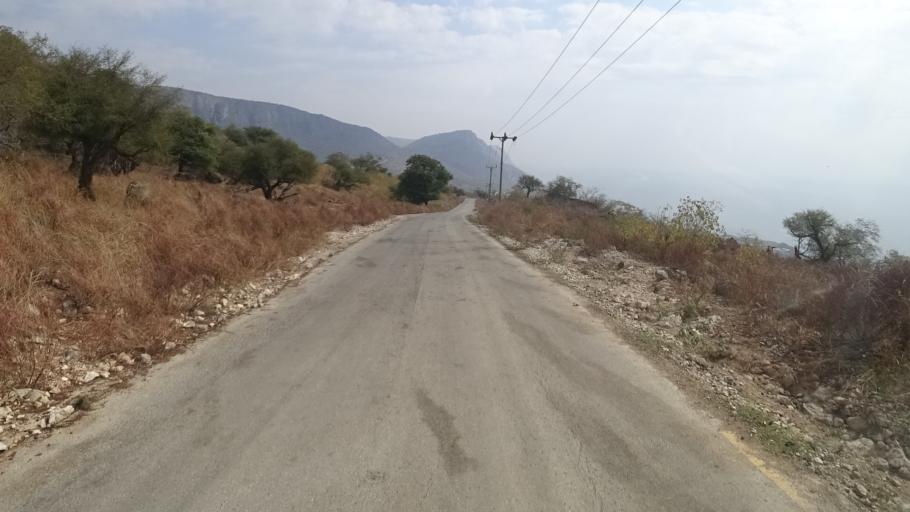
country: YE
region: Al Mahrah
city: Hawf
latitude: 16.7099
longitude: 53.2425
